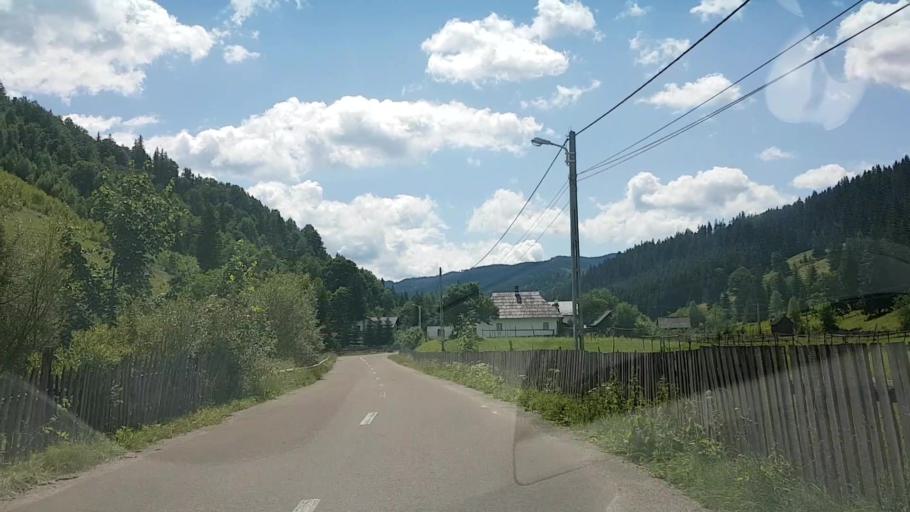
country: RO
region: Suceava
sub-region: Comuna Pojorata
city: Pojorata
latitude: 47.4950
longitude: 25.4826
